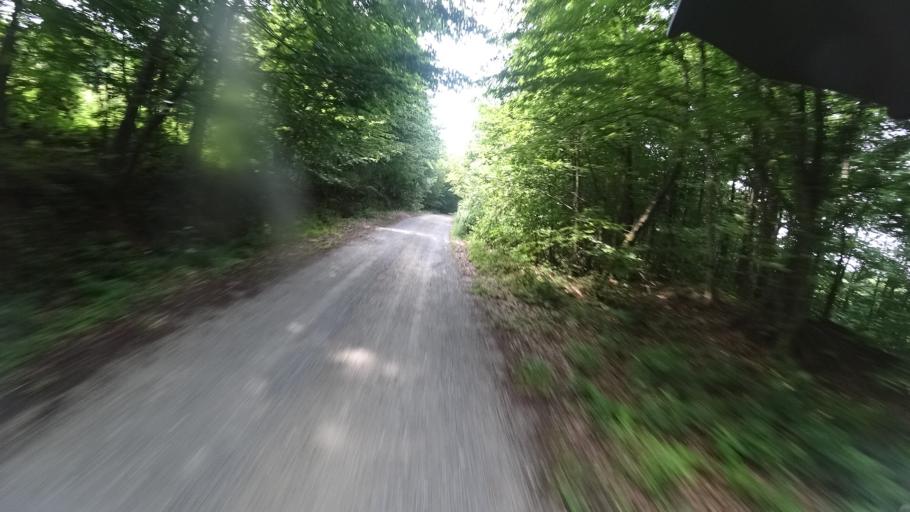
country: HR
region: Sisacko-Moslavacka
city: Gvozd
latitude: 45.3293
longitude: 15.8402
